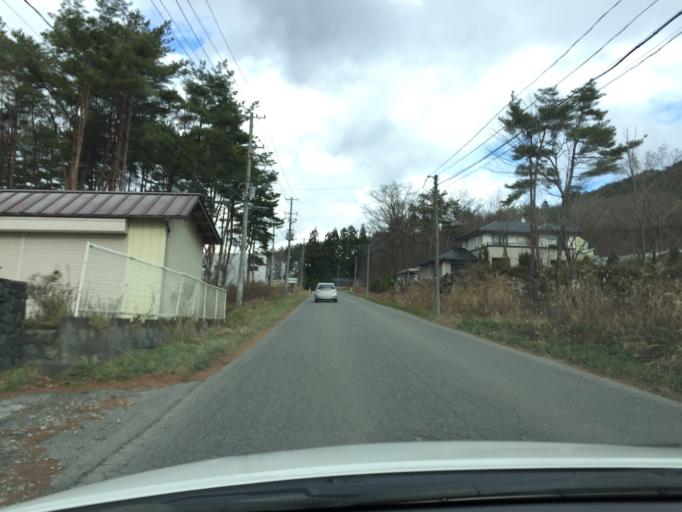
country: JP
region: Fukushima
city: Yanagawamachi-saiwaicho
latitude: 37.6974
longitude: 140.6975
